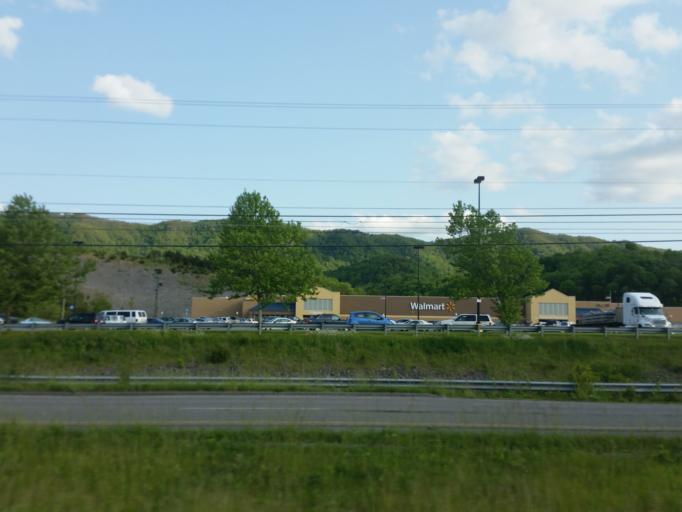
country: US
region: Virginia
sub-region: Tazewell County
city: Claypool Hill
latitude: 37.0676
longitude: -81.7324
